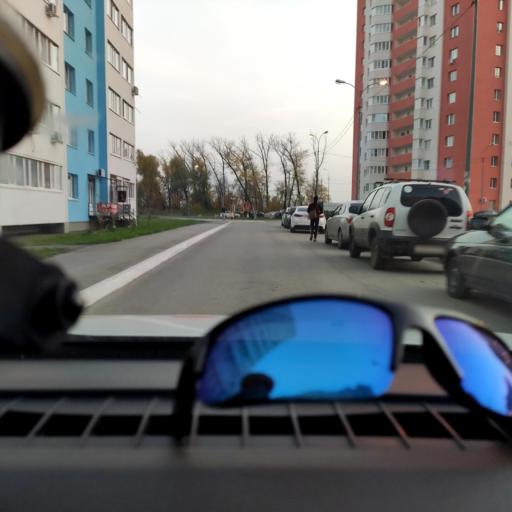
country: RU
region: Samara
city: Samara
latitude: 53.1478
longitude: 50.0787
